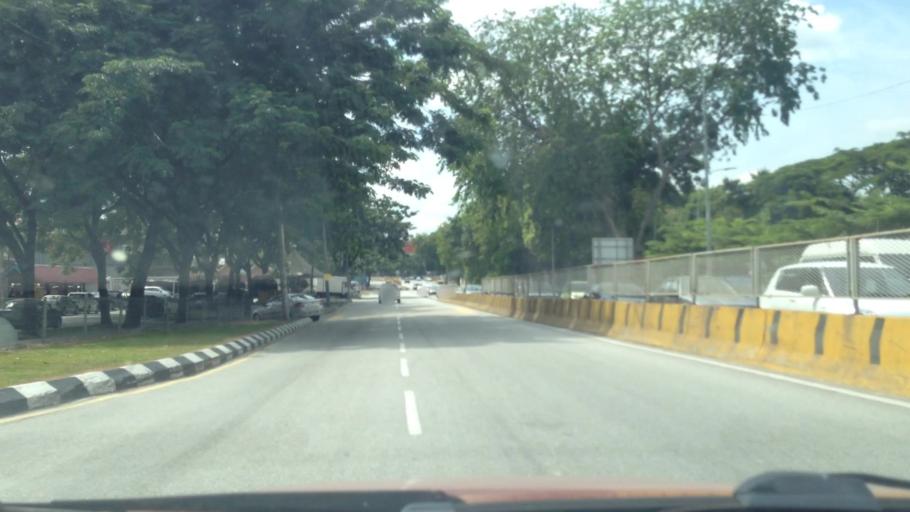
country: MY
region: Kuala Lumpur
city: Kuala Lumpur
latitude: 3.0923
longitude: 101.6838
